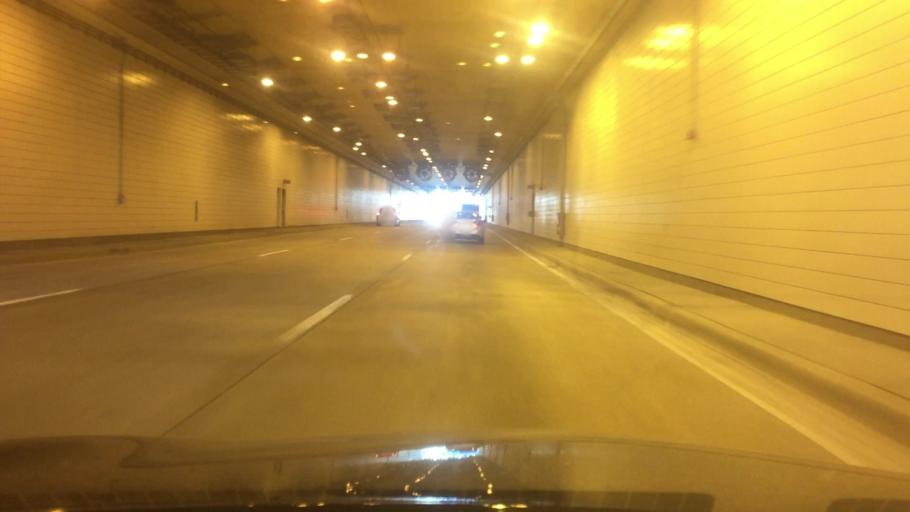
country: US
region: Michigan
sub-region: Wayne County
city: Romulus
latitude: 42.2183
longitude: -83.3465
